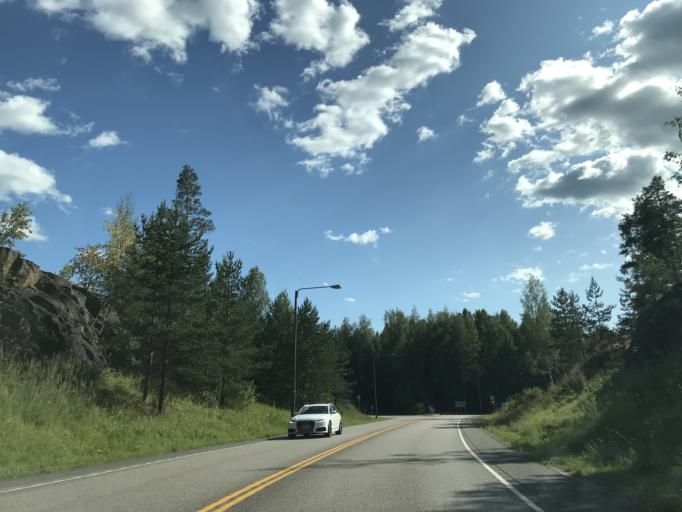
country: FI
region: Uusimaa
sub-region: Helsinki
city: Nurmijaervi
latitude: 60.4584
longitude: 24.8355
